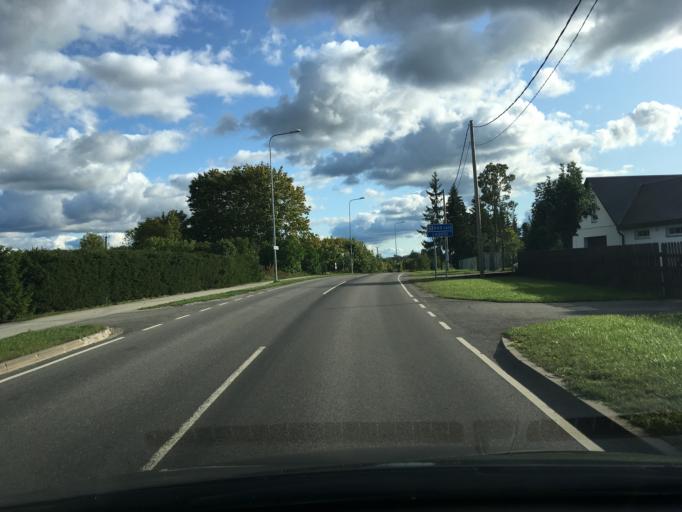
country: EE
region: Harju
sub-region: Joelaehtme vald
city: Loo
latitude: 59.4126
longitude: 24.9475
